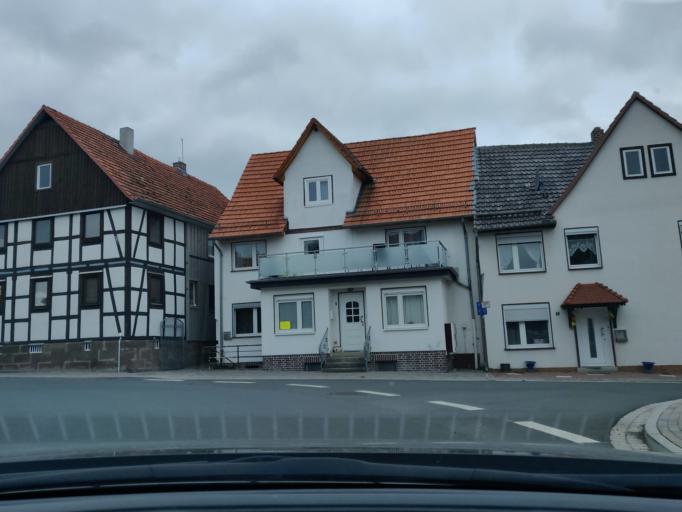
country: DE
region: Hesse
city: Fritzlar
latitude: 51.1798
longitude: 9.2684
